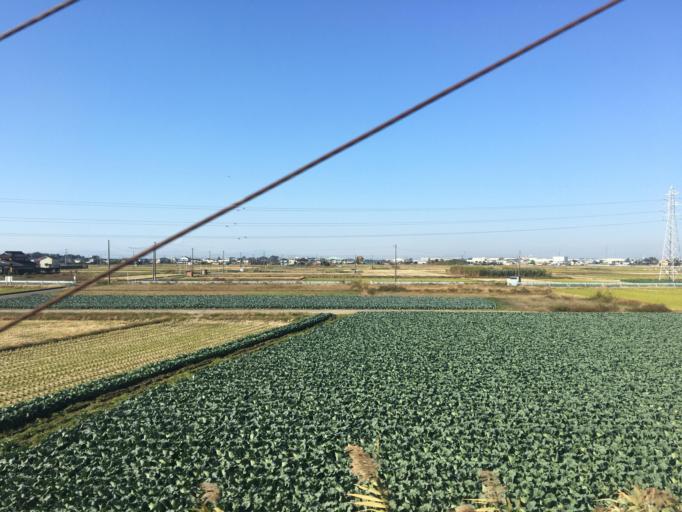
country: JP
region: Saitama
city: Hanyu
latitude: 36.2008
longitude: 139.5261
